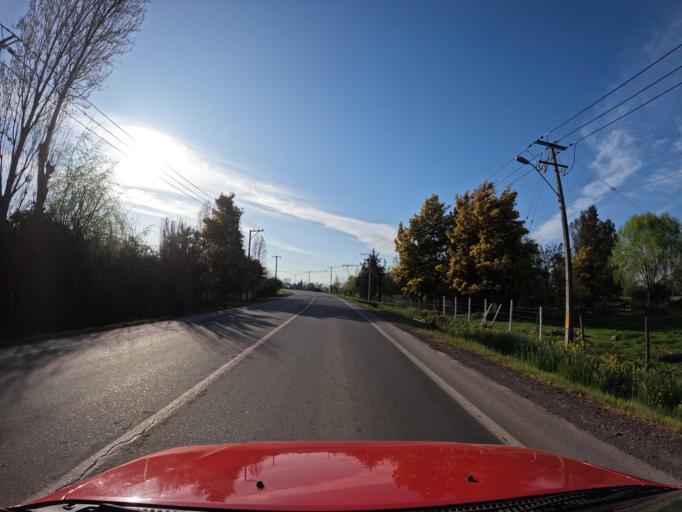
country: CL
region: Maule
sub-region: Provincia de Curico
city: Teno
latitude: -34.9003
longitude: -71.0568
